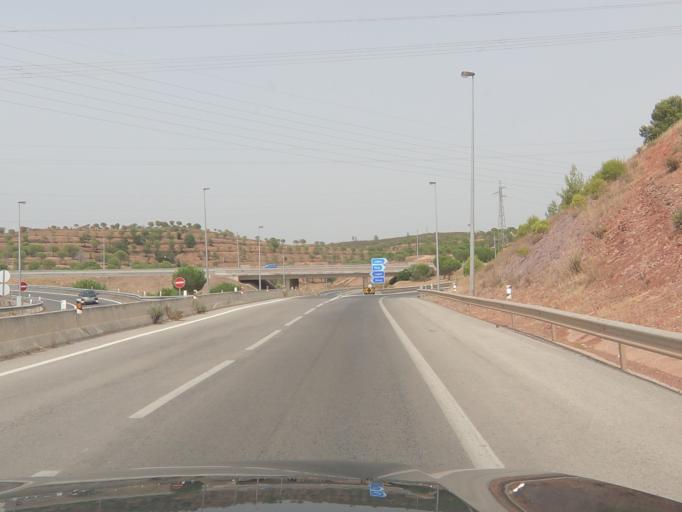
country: PT
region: Faro
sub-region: Portimao
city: Portimao
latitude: 37.1767
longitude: -8.5303
